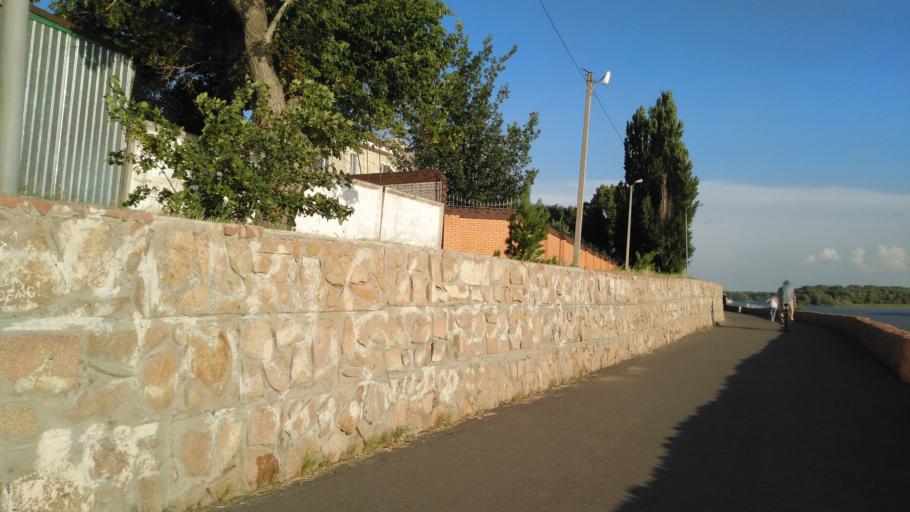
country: KZ
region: Pavlodar
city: Pavlodar
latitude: 52.2776
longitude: 76.9332
